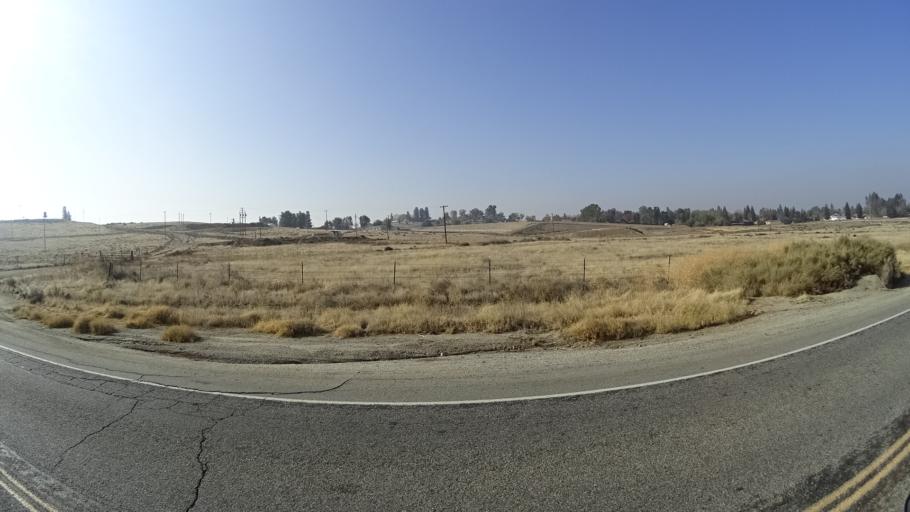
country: US
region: California
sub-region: Kern County
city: Lamont
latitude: 35.4026
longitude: -118.8584
